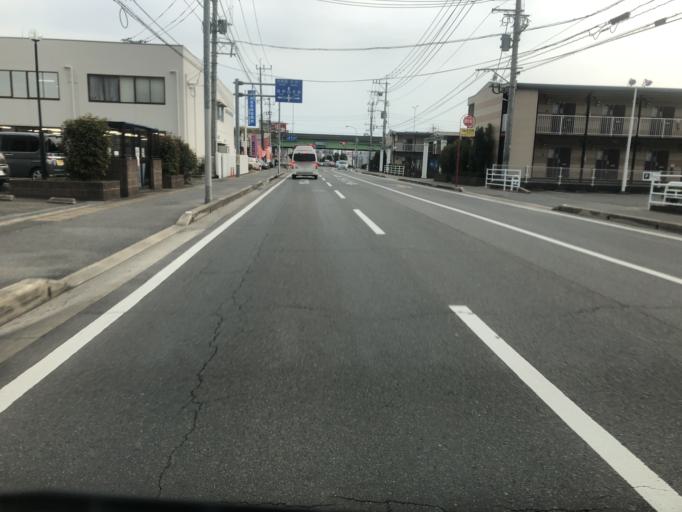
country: JP
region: Saga Prefecture
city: Saga-shi
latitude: 33.2735
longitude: 130.2709
